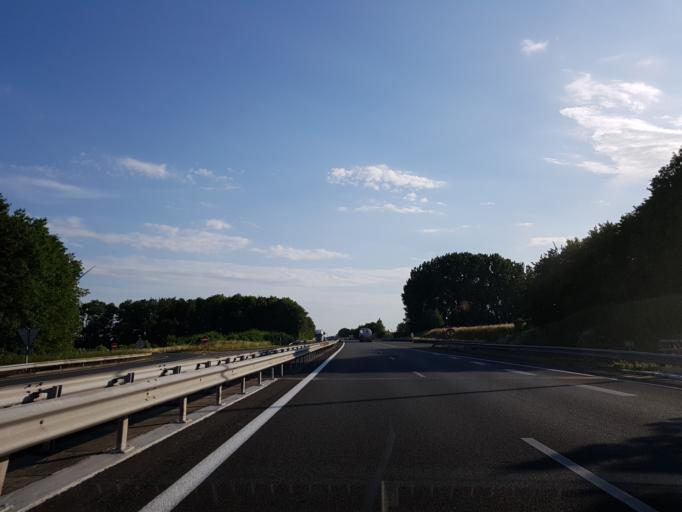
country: FR
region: Nord-Pas-de-Calais
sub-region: Departement du Pas-de-Calais
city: Bourlon
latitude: 50.1443
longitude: 3.1269
